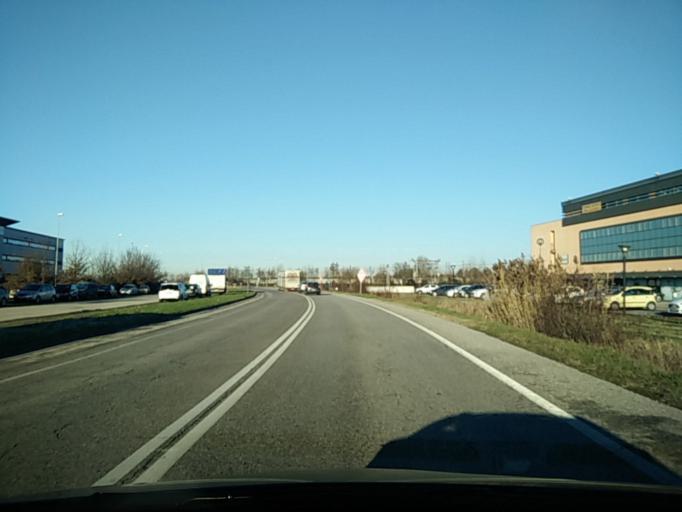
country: IT
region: Veneto
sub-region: Provincia di Venezia
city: Ballo
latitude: 45.4510
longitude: 12.0662
